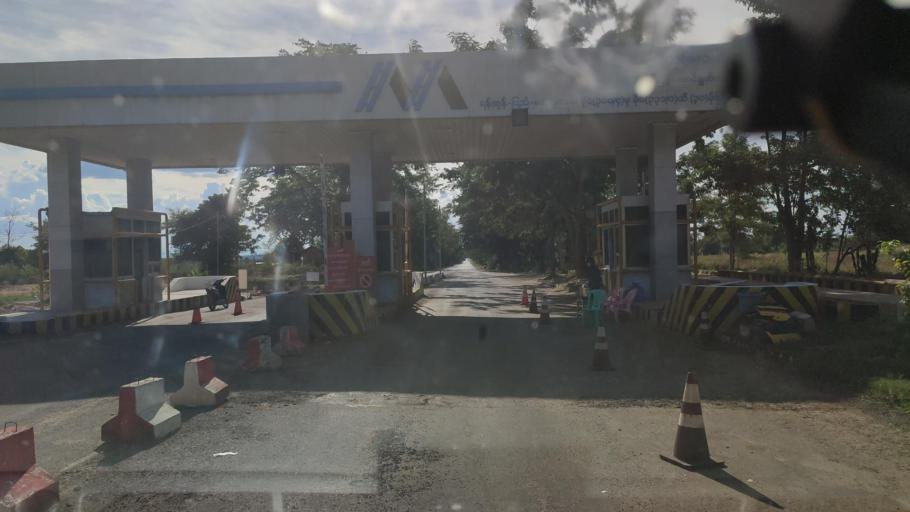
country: MM
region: Magway
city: Magway
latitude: 20.1227
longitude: 95.0082
